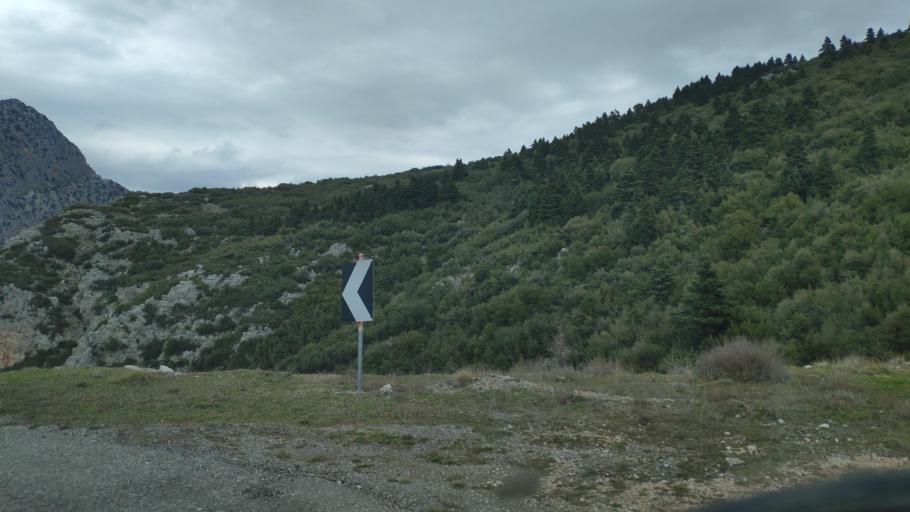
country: GR
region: Central Greece
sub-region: Nomos Fokidos
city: Amfissa
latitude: 38.6448
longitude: 22.4199
